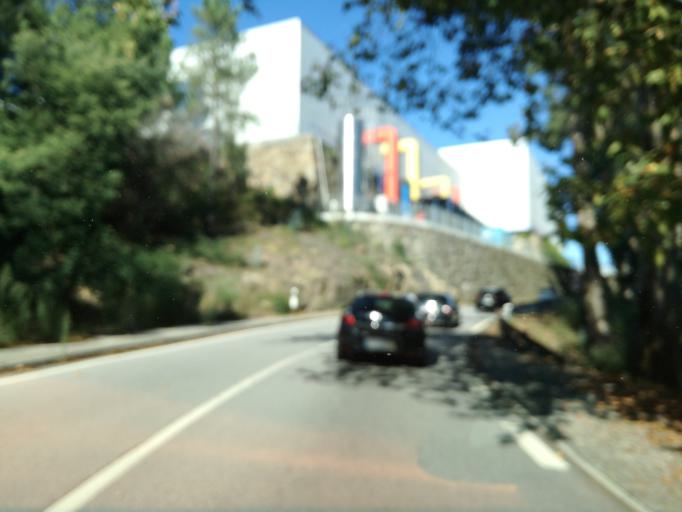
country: PT
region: Porto
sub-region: Pacos de Ferreira
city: Seroa
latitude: 41.2573
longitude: -8.4462
